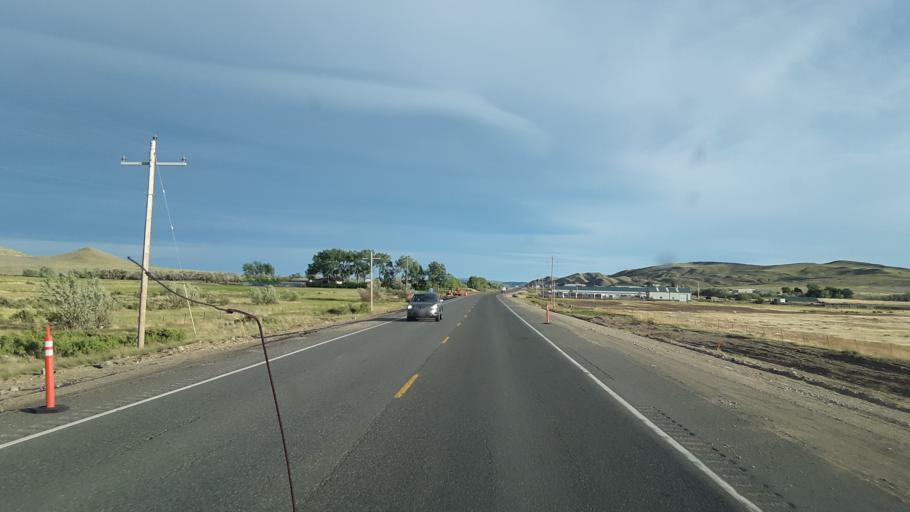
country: US
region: Wyoming
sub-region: Park County
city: Cody
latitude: 44.5063
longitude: -109.0256
